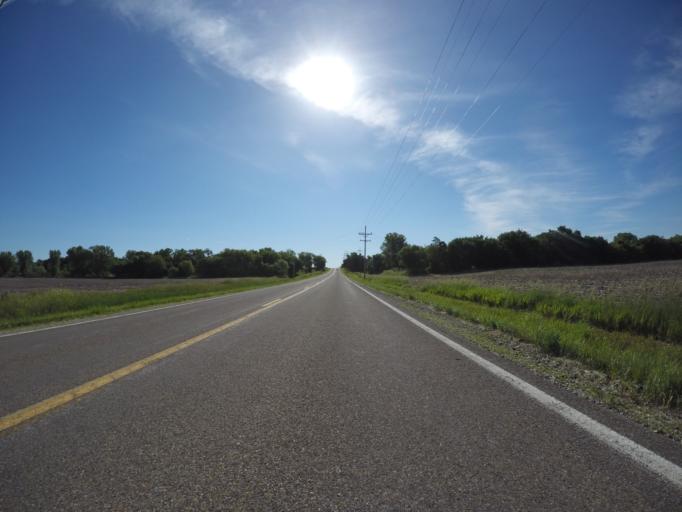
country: US
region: Kansas
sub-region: Mitchell County
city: Beloit
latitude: 39.6393
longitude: -97.9465
